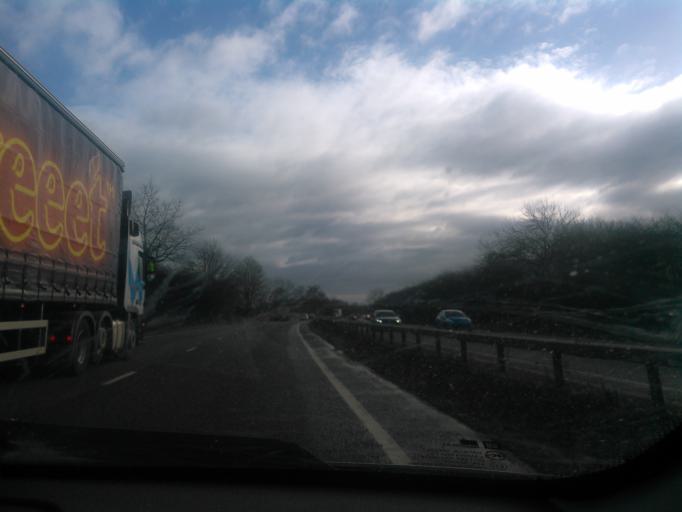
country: GB
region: England
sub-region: Derbyshire
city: Rodsley
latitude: 52.8900
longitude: -1.7644
